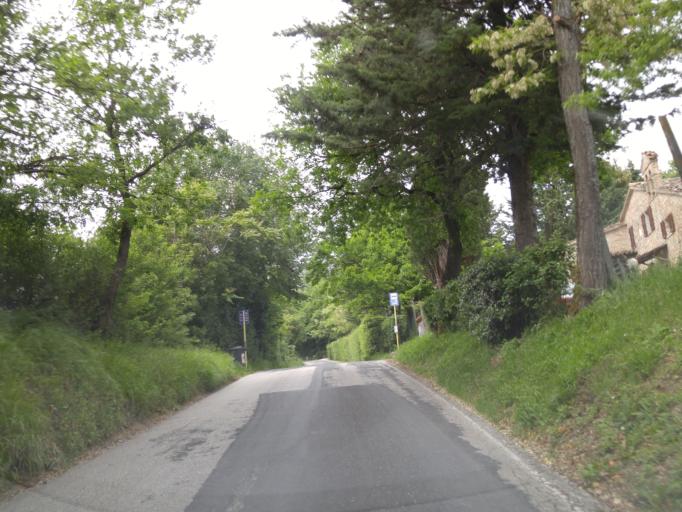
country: IT
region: The Marches
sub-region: Provincia di Pesaro e Urbino
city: Urbino
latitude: 43.7122
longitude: 12.6341
